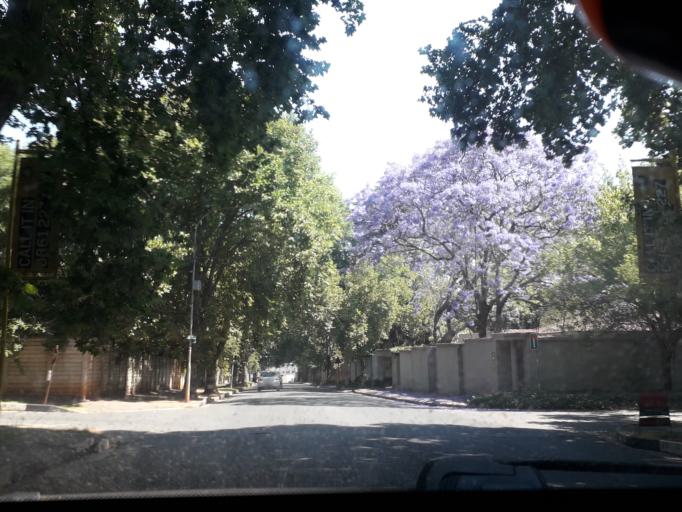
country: ZA
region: Gauteng
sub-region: City of Johannesburg Metropolitan Municipality
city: Johannesburg
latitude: -26.1443
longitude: 28.0669
